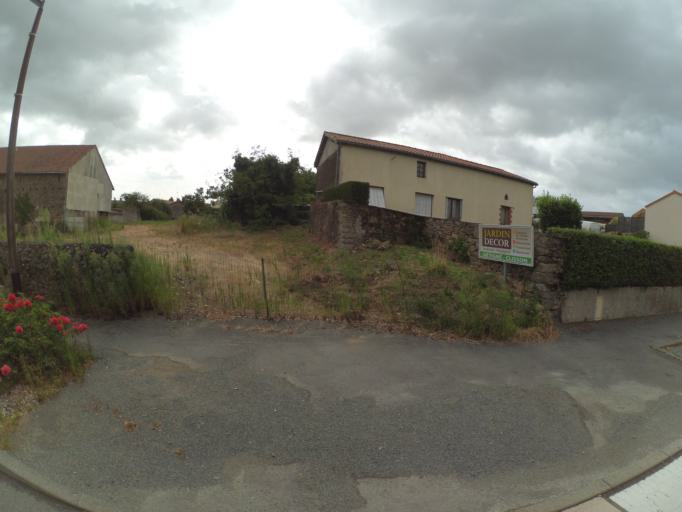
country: FR
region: Pays de la Loire
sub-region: Departement de Maine-et-Loire
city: Montfaucon-Montigne
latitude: 47.0961
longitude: -1.1271
